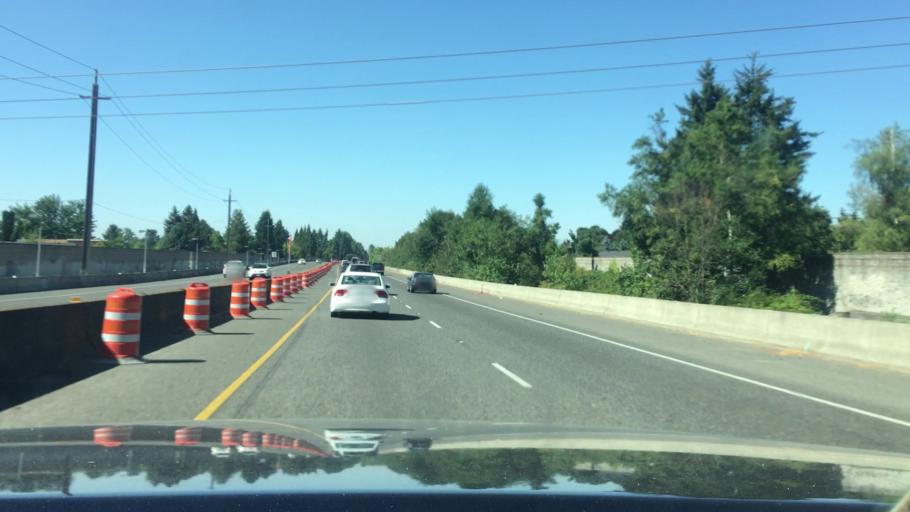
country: US
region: Oregon
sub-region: Lane County
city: Eugene
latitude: 44.0734
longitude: -123.1735
